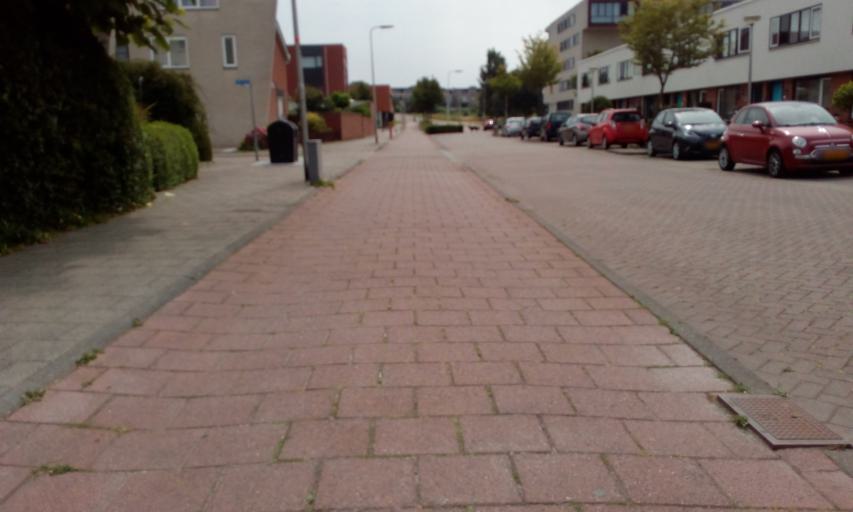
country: NL
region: South Holland
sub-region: Gemeente Krimpen aan den IJssel
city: Krimpen aan den IJssel
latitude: 51.9619
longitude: 4.6140
